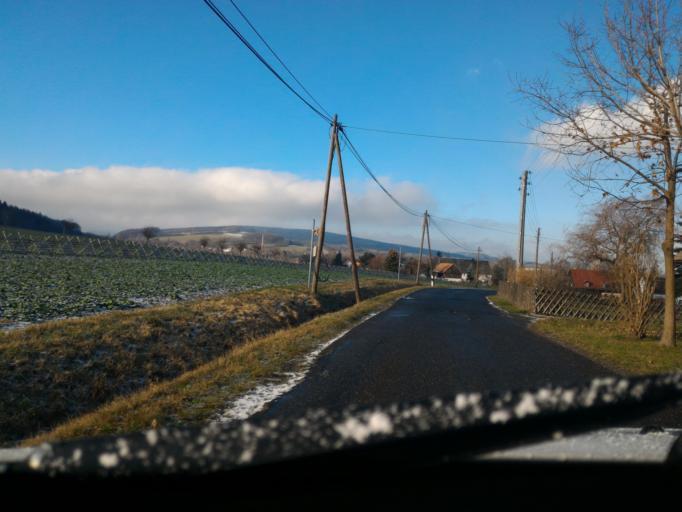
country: CZ
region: Ustecky
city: Varnsdorf
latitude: 50.8771
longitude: 14.6404
